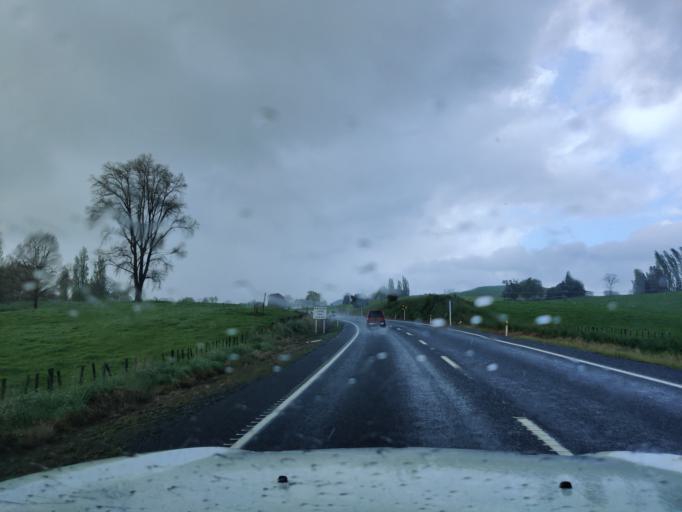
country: NZ
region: Waikato
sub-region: Matamata-Piako District
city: Matamata
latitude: -37.9816
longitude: 175.7035
